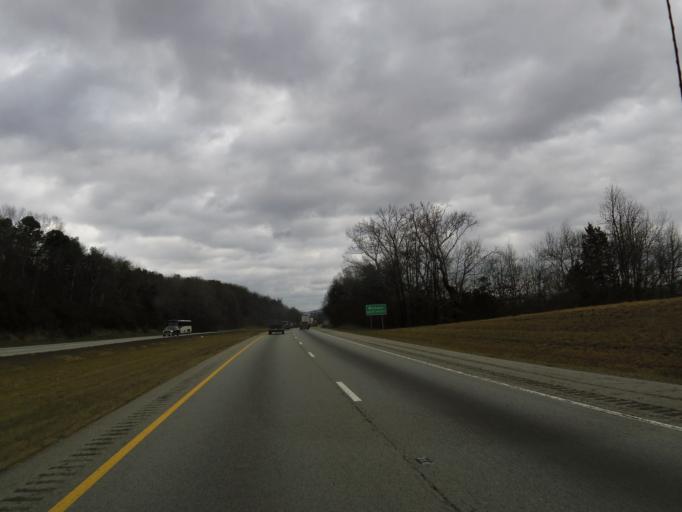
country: US
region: Tennessee
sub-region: Marion County
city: Kimball
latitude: 35.0503
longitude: -85.6471
